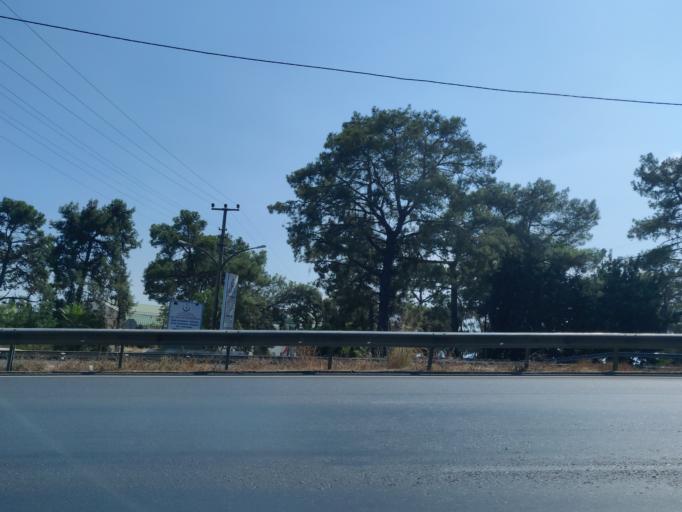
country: TR
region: Antalya
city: Dosemealti
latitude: 36.9505
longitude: 30.6279
